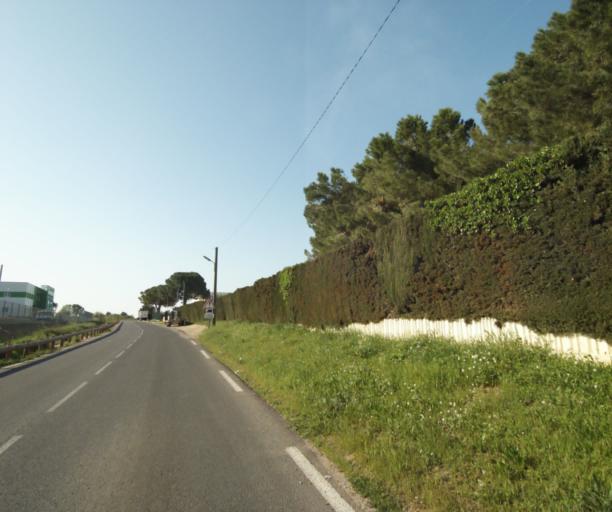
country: FR
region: Languedoc-Roussillon
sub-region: Departement de l'Herault
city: Laverune
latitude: 43.5918
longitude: 3.7995
